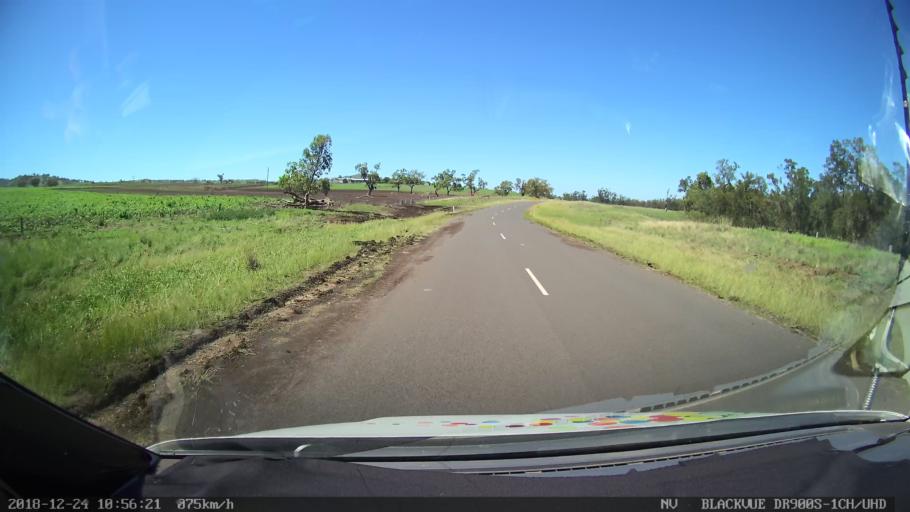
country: AU
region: New South Wales
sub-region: Upper Hunter Shire
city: Merriwa
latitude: -32.0248
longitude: 150.4185
